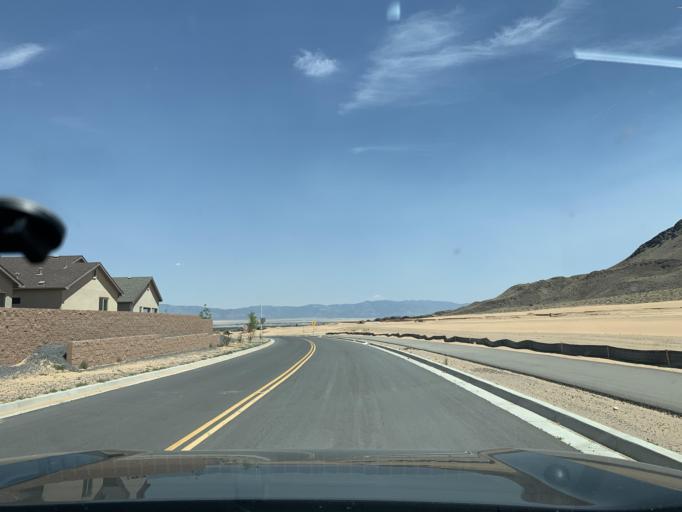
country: US
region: New Mexico
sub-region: Valencia County
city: Los Lunas
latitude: 34.8183
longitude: -106.8003
